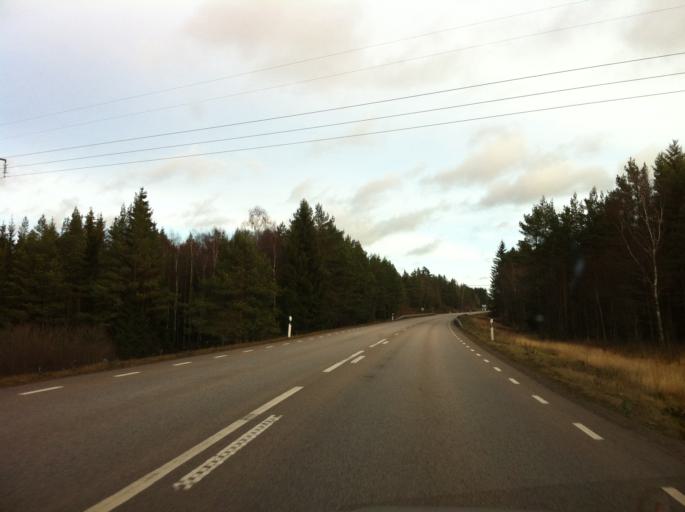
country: SE
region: Kronoberg
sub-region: Uppvidinge Kommun
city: Aseda
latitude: 57.1243
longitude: 15.2640
